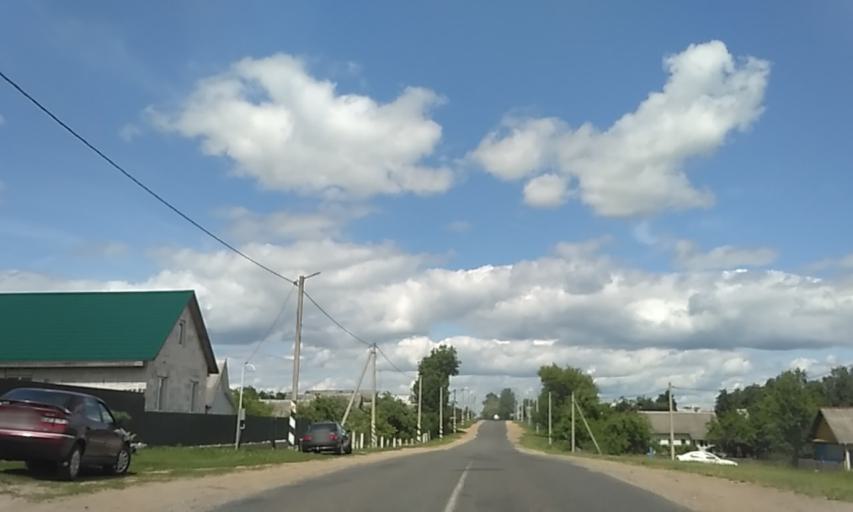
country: BY
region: Minsk
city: Krupki
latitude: 54.3468
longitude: 29.1512
